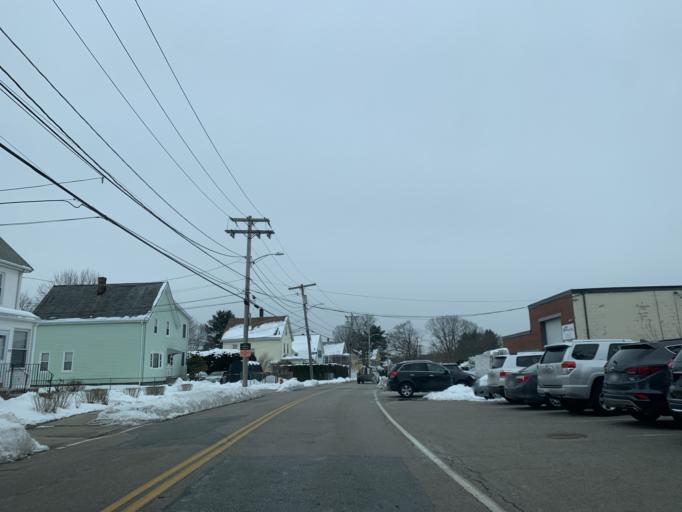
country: US
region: Massachusetts
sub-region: Norfolk County
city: Norwood
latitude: 42.1862
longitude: -71.1987
